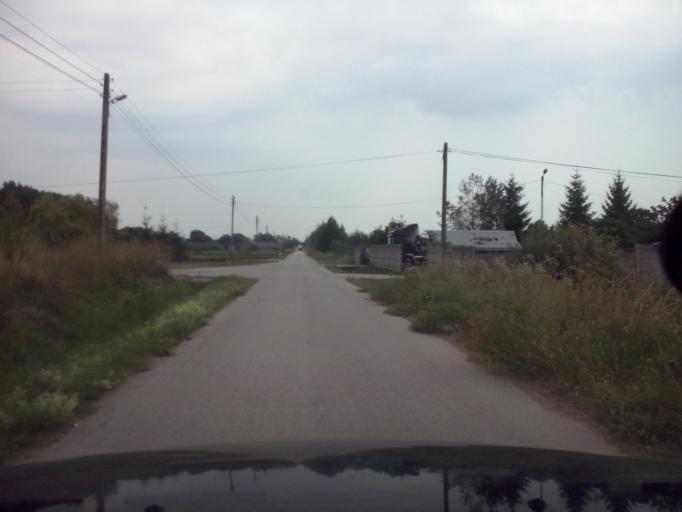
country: PL
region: Swietokrzyskie
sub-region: Powiat kielecki
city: Brzeziny
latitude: 50.7821
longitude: 20.5526
